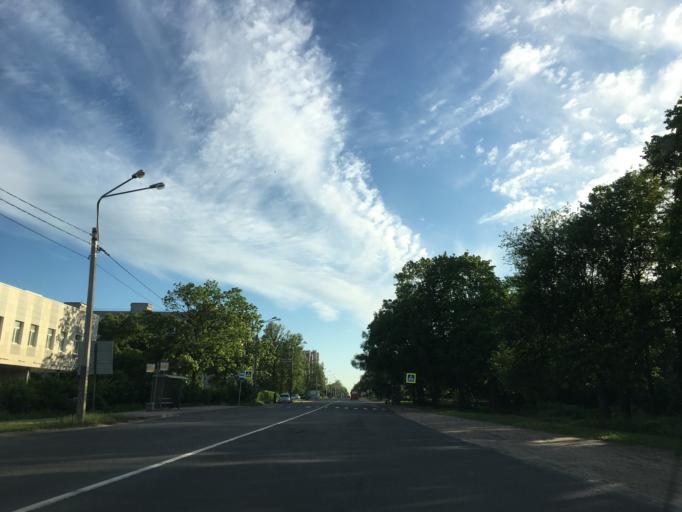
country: RU
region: St.-Petersburg
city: Krasnoye Selo
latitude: 59.7239
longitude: 30.0777
